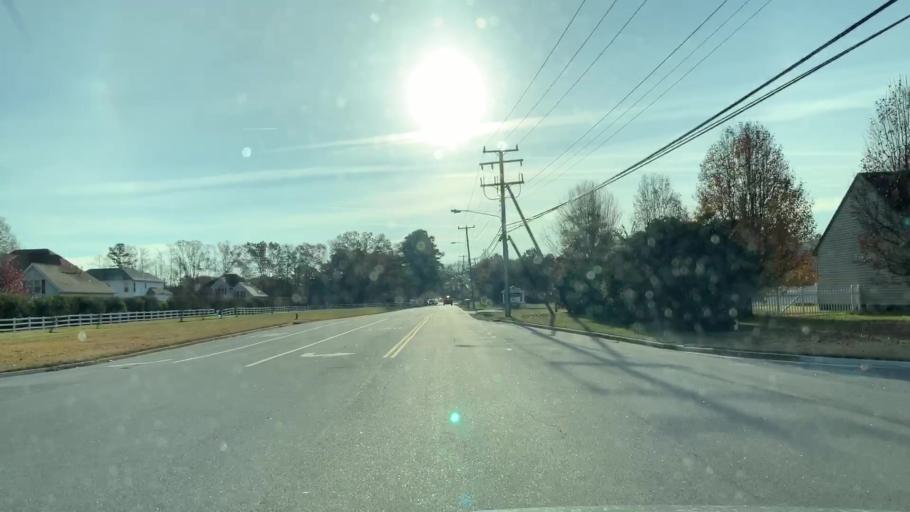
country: US
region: Virginia
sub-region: City of Chesapeake
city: Chesapeake
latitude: 36.7579
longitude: -76.1356
